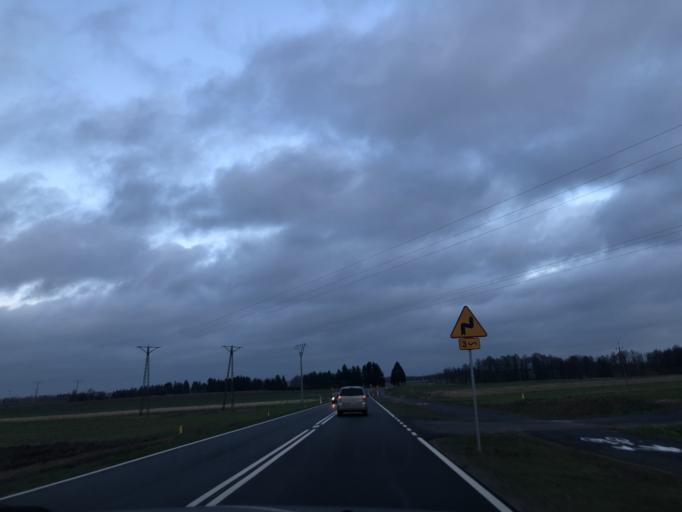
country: PL
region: Podlasie
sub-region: Lomza
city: Lomza
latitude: 53.1233
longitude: 22.0406
